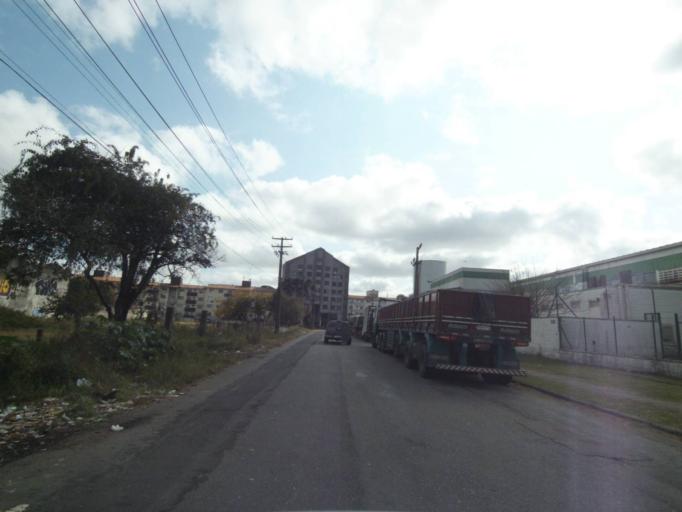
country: BR
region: Parana
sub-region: Curitiba
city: Curitiba
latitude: -25.4692
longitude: -49.2577
